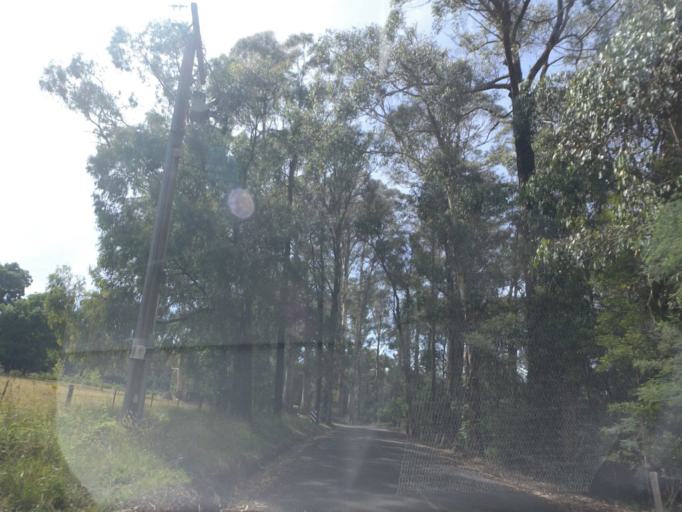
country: AU
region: Victoria
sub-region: Yarra Ranges
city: Yarra Glen
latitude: -37.5120
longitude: 145.4256
